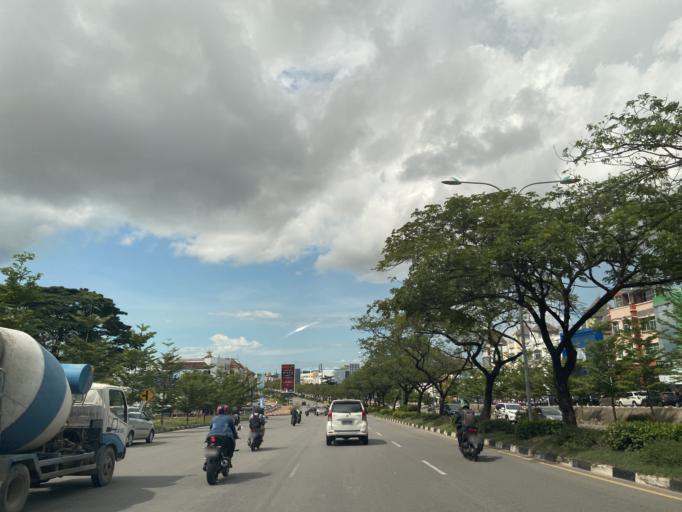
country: SG
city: Singapore
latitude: 1.1278
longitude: 104.0350
